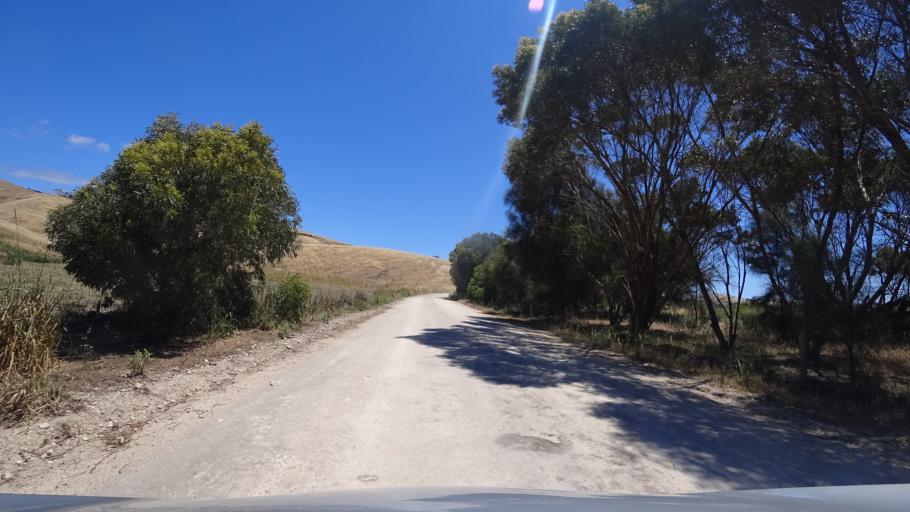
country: AU
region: South Australia
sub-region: Kangaroo Island
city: Kingscote
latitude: -35.6698
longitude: 137.0760
